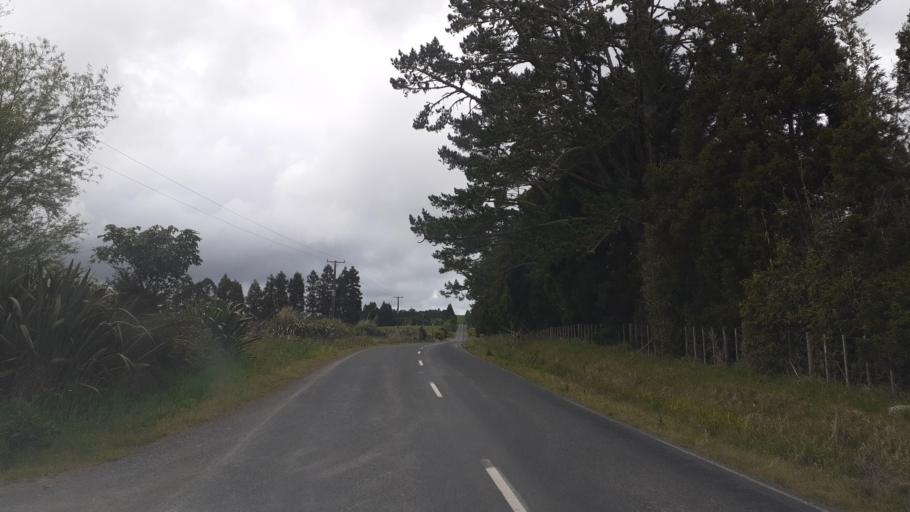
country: NZ
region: Northland
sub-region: Far North District
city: Waimate North
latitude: -35.2581
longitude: 173.8036
